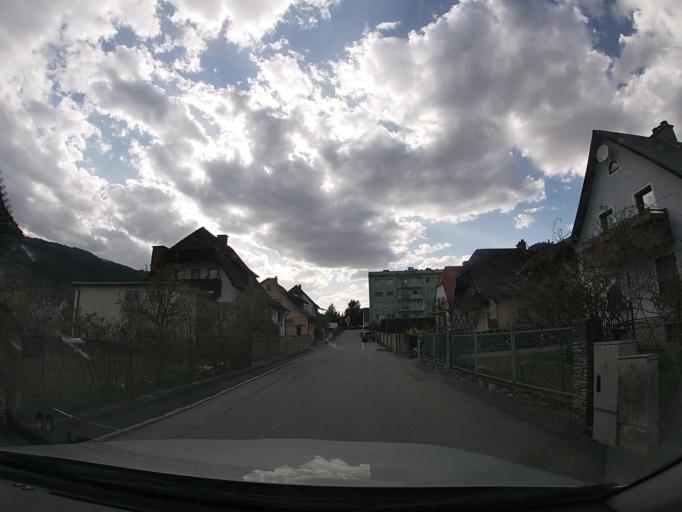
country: AT
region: Styria
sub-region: Politischer Bezirk Murau
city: Murau
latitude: 47.1112
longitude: 14.1806
